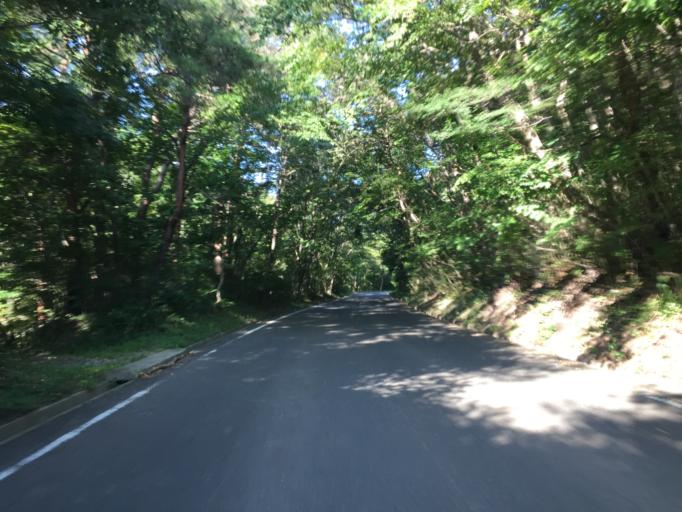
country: JP
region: Fukushima
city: Fukushima-shi
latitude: 37.7239
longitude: 140.5189
